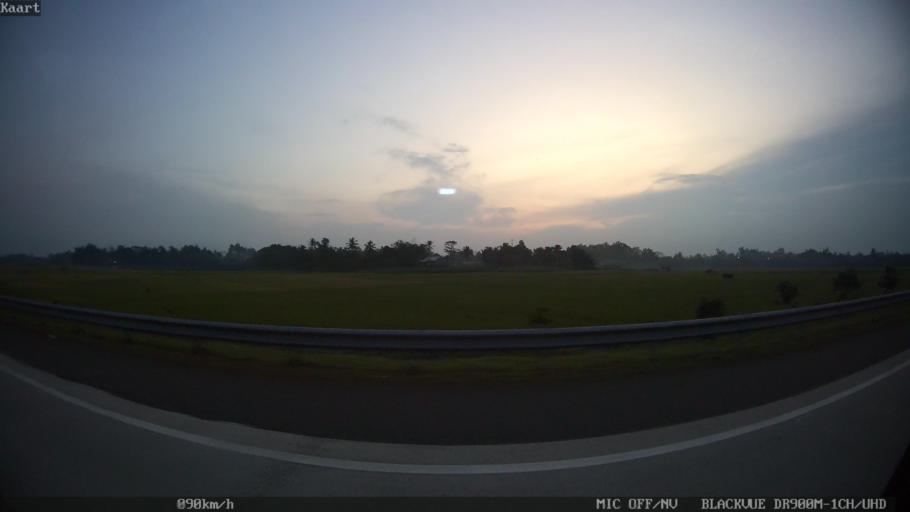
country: ID
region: Lampung
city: Sidorejo
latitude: -5.5759
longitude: 105.5404
